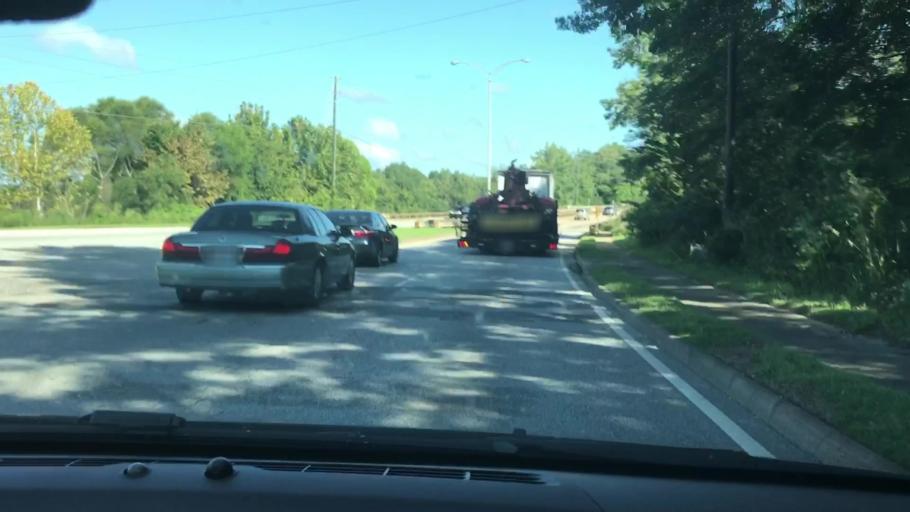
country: US
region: Alabama
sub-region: Barbour County
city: Eufaula
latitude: 31.9059
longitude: -85.1490
